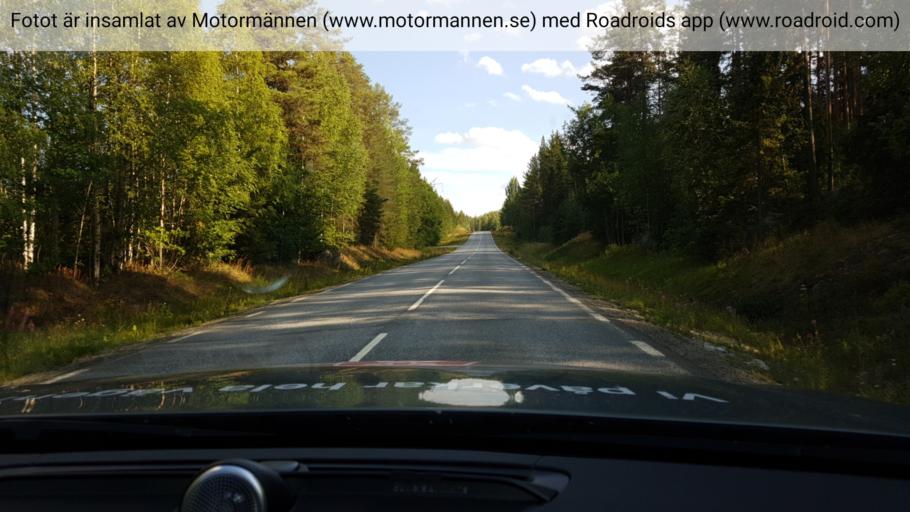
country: SE
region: Vaesterbotten
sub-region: Dorotea Kommun
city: Dorotea
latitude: 63.8945
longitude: 16.3629
